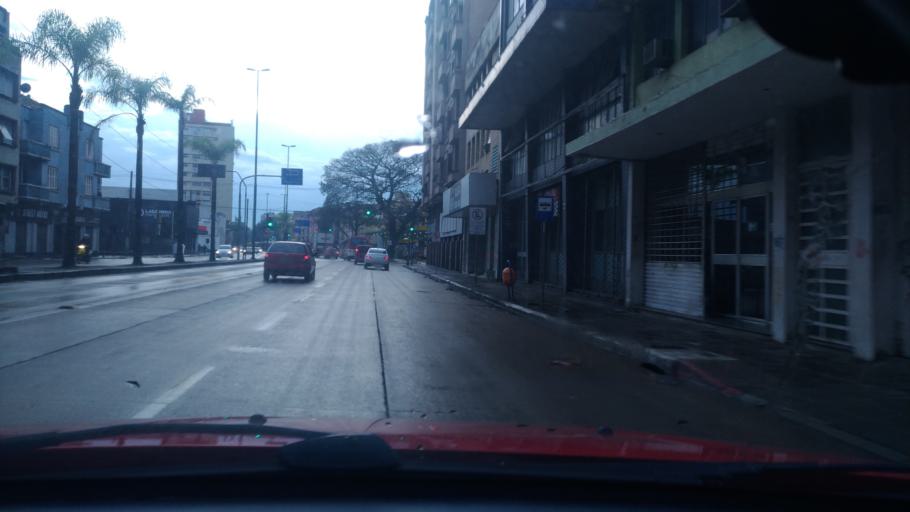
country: BR
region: Rio Grande do Sul
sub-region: Porto Alegre
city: Porto Alegre
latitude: -30.0263
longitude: -51.2167
